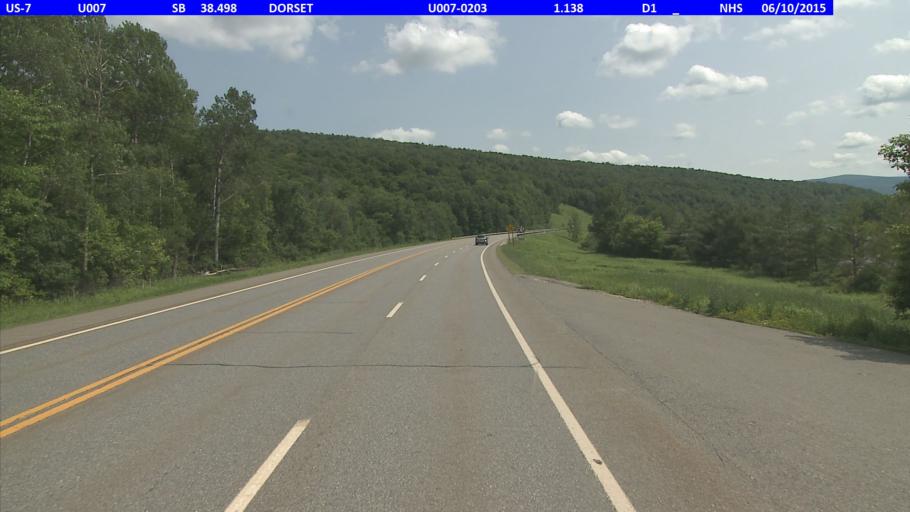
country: US
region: Vermont
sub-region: Bennington County
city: Manchester Center
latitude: 43.2270
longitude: -73.0075
